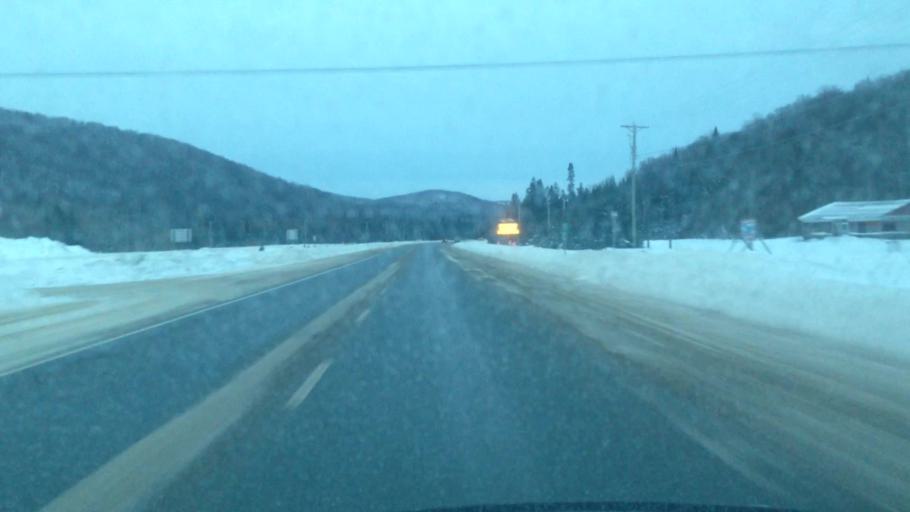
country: CA
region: Quebec
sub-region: Laurentides
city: Mont-Tremblant
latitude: 46.1232
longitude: -74.4503
